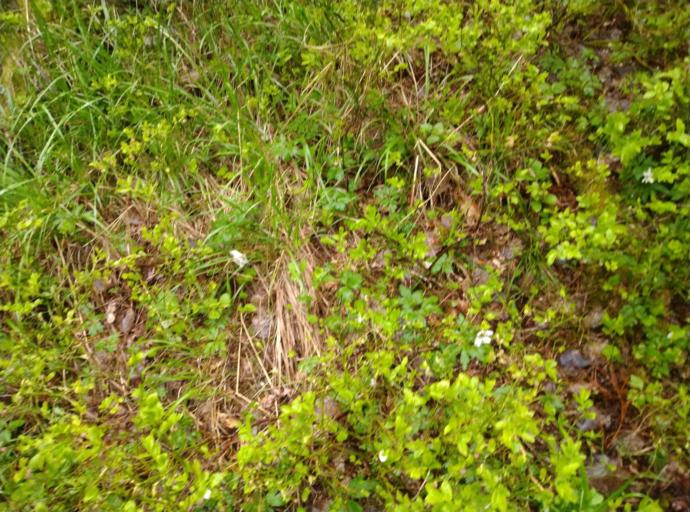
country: SE
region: Stockholm
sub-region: Nacka Kommun
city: Fisksatra
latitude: 59.2961
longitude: 18.2827
